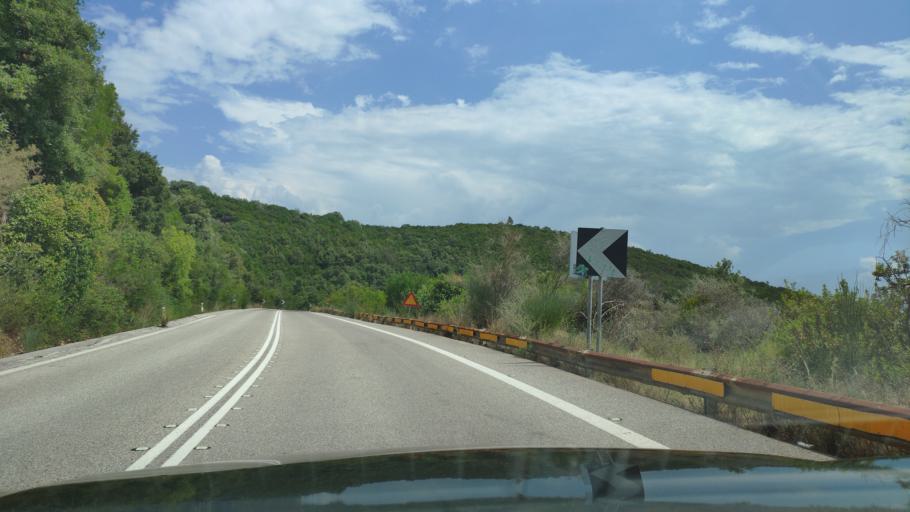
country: GR
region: West Greece
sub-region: Nomos Aitolias kai Akarnanias
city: Menidi
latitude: 39.0374
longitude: 21.1191
